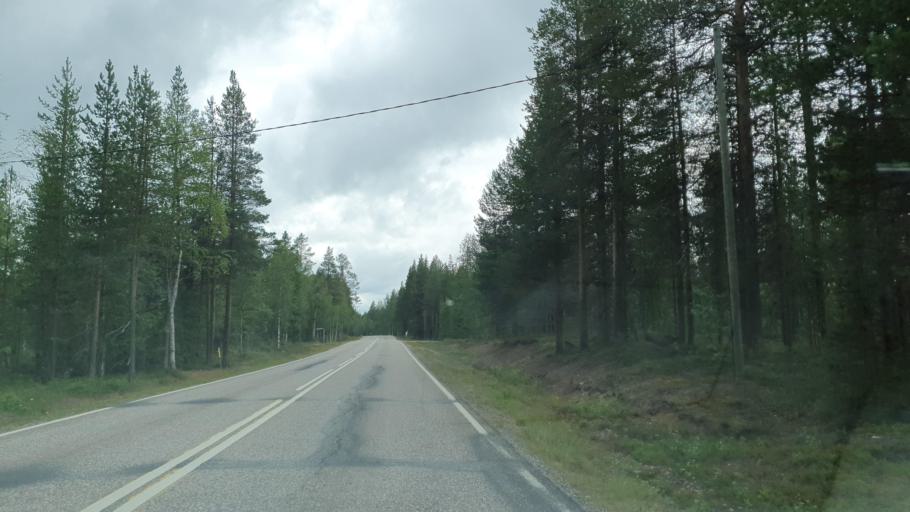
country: FI
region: Lapland
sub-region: Tunturi-Lappi
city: Kolari
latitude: 67.5104
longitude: 24.2798
